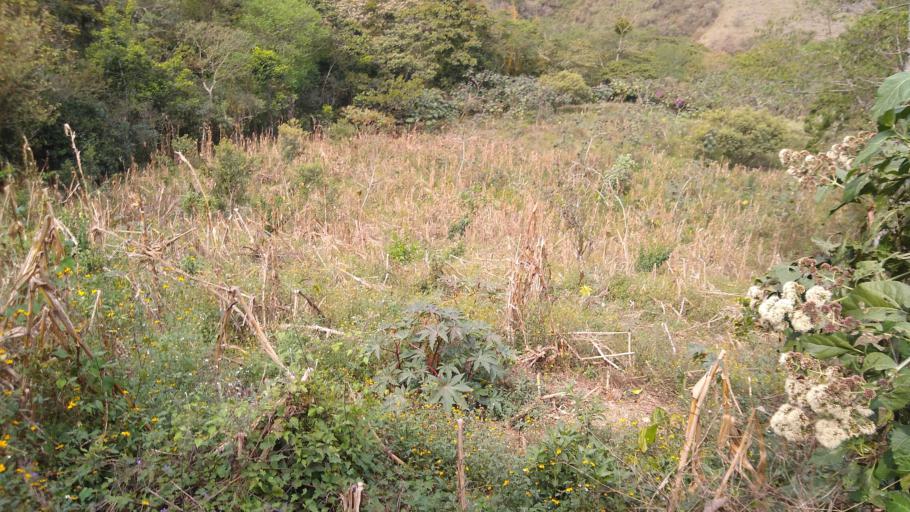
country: MX
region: Puebla
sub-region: Tepetzintla
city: Tlamanca de Hernandez
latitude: 19.9334
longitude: -97.8131
